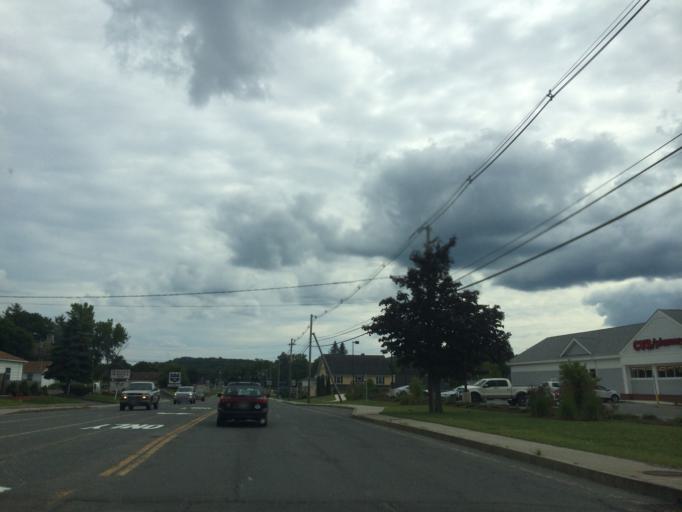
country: US
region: Massachusetts
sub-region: Berkshire County
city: Pittsfield
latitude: 42.4047
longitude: -73.2653
